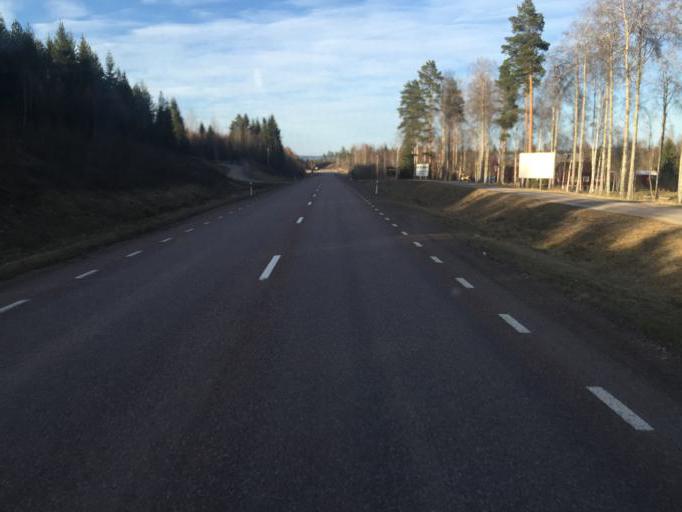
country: SE
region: Dalarna
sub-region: Gagnefs Kommun
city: Gagnef
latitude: 60.5357
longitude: 15.0475
